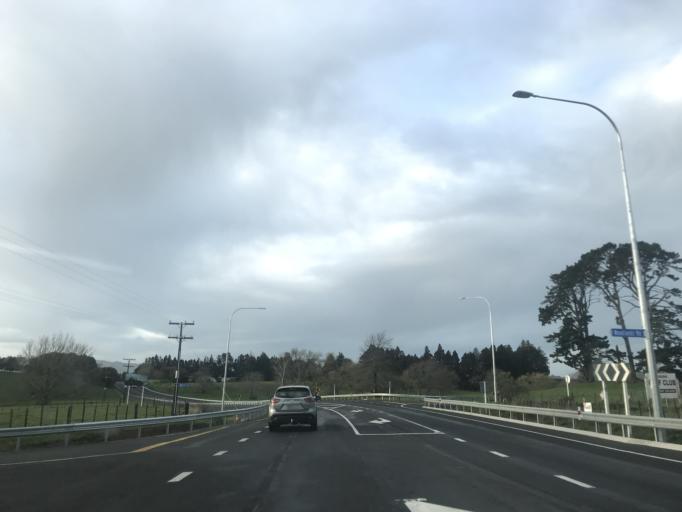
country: NZ
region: Waikato
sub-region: Hauraki District
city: Waihi
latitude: -37.4359
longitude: 175.8734
